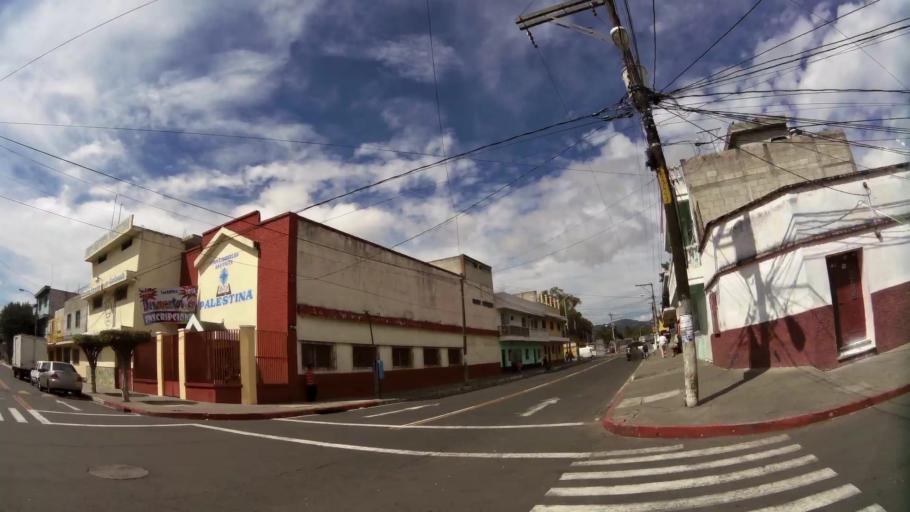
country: GT
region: Guatemala
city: Mixco
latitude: 14.6569
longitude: -90.5808
